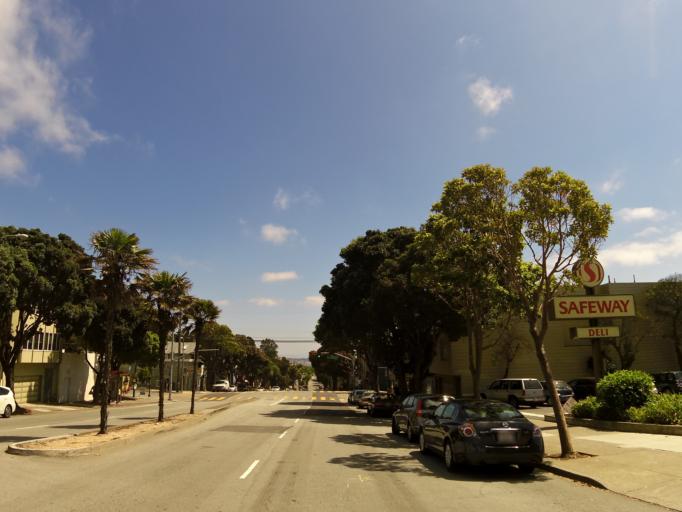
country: US
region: California
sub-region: San Mateo County
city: Daly City
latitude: 37.7315
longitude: -122.4498
